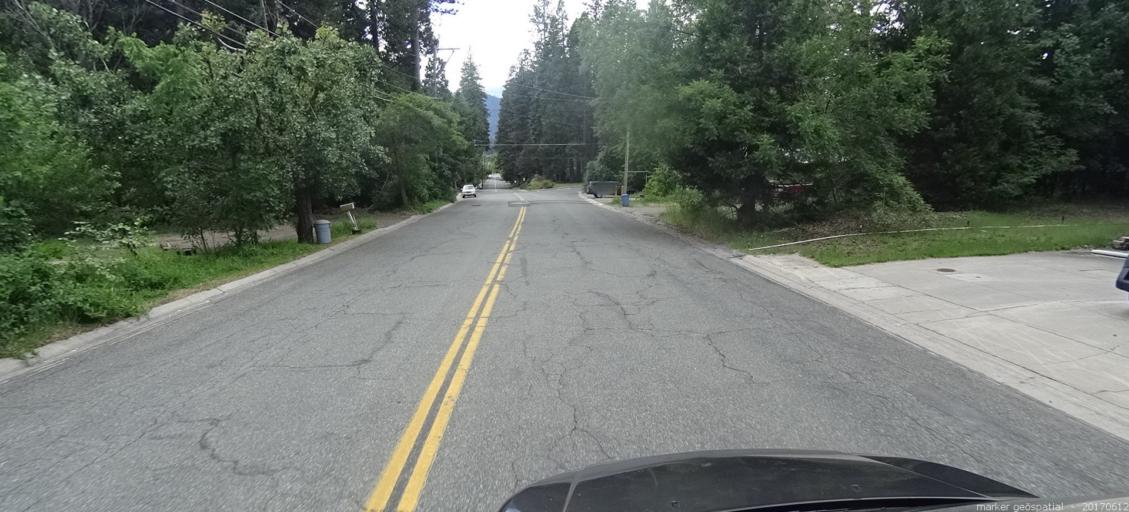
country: US
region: California
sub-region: Siskiyou County
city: Mount Shasta
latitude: 41.3123
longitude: -122.3050
